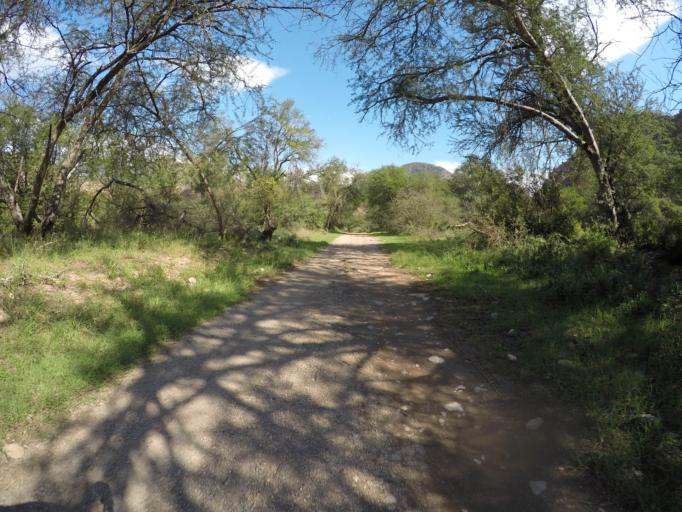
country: ZA
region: Eastern Cape
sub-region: Cacadu District Municipality
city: Kareedouw
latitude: -33.6652
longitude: 24.3872
